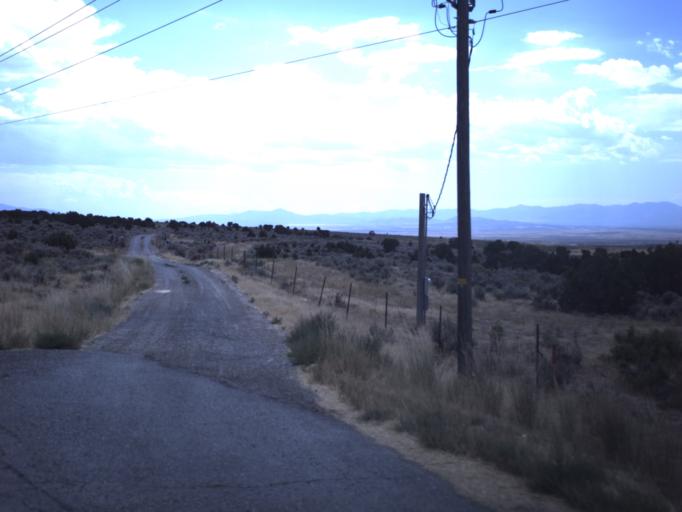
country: US
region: Utah
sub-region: Tooele County
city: Tooele
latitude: 40.3420
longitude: -112.3038
